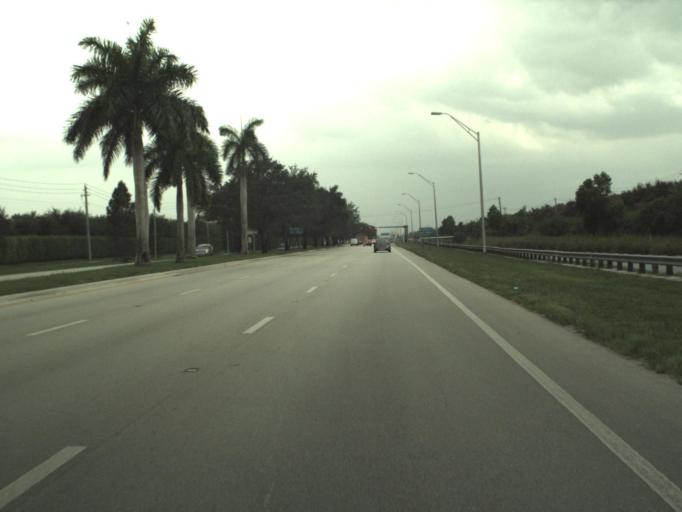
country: US
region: Florida
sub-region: Broward County
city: Sunshine Ranches
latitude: 26.0041
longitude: -80.3120
